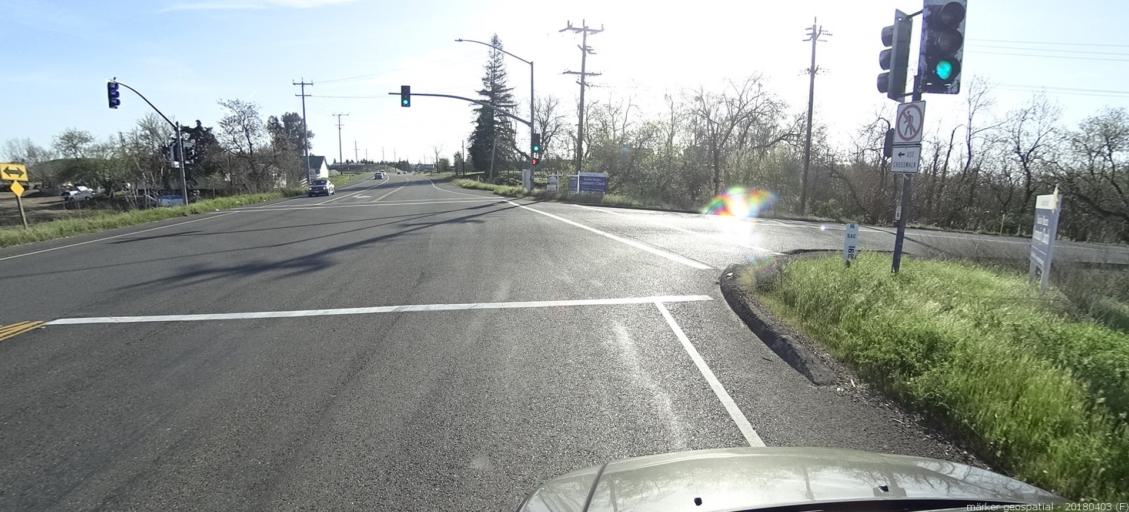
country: US
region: California
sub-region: Sacramento County
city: Rancho Murieta
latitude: 38.4932
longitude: -121.1615
